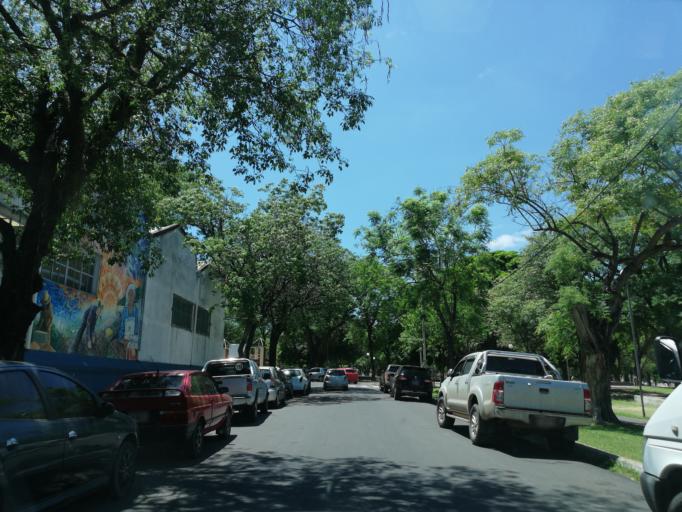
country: AR
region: Corrientes
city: Corrientes
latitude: -27.4592
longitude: -58.8305
